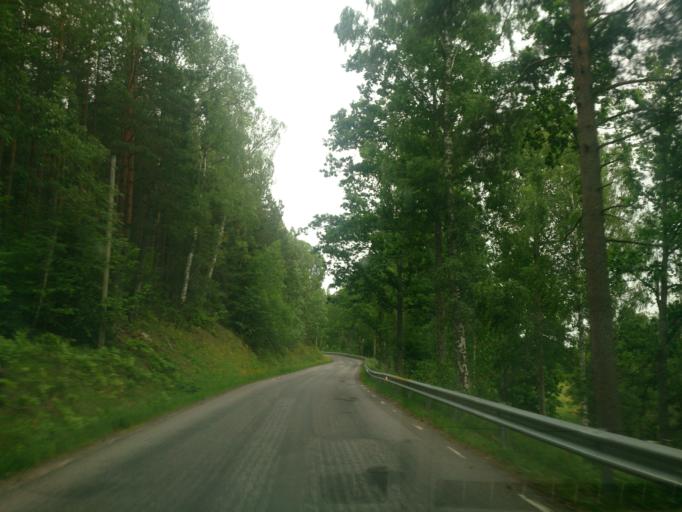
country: SE
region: OEstergoetland
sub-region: Atvidabergs Kommun
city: Atvidaberg
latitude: 58.2805
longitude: 16.1535
